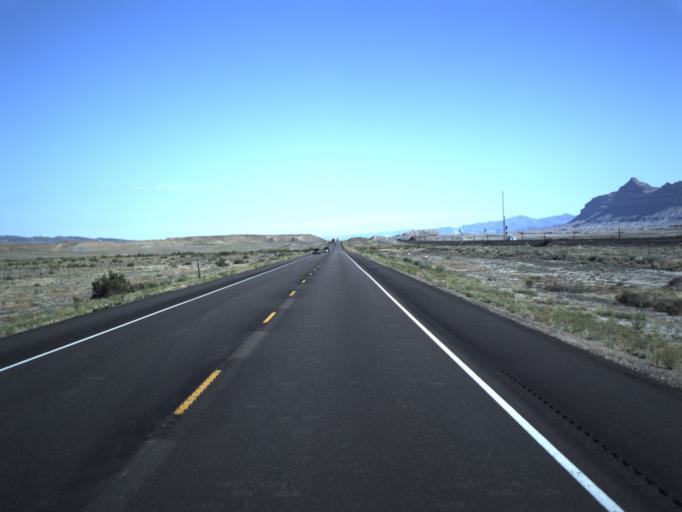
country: US
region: Utah
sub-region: Carbon County
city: East Carbon City
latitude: 39.0754
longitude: -110.3166
